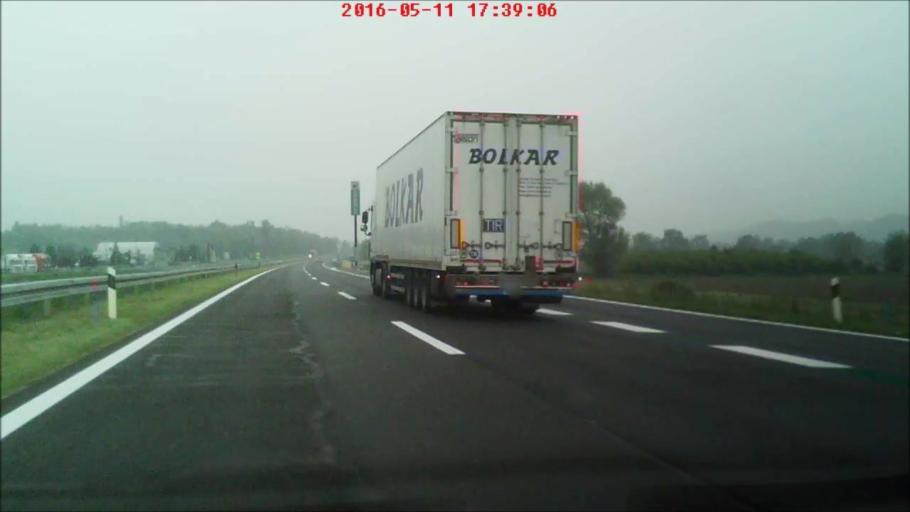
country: HR
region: Krapinsko-Zagorska
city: Zabok
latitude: 46.0711
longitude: 15.9188
